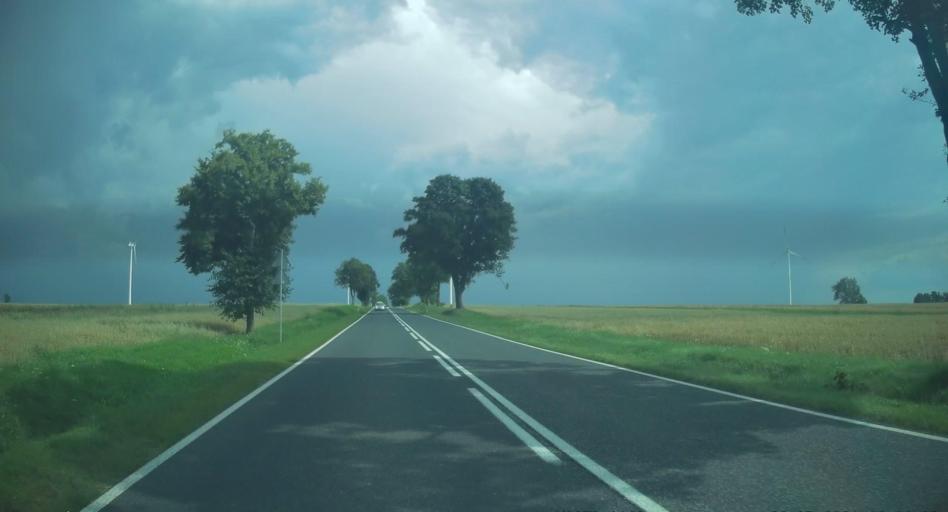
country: PL
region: Lodz Voivodeship
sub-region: Powiat skierniewicki
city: Gluchow
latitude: 51.7970
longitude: 20.0296
